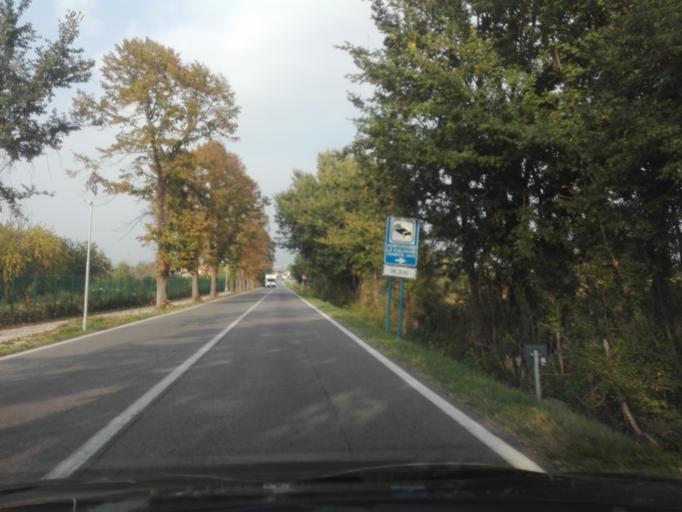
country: IT
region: Veneto
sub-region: Provincia di Verona
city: Lazise
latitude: 45.4898
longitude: 10.7371
